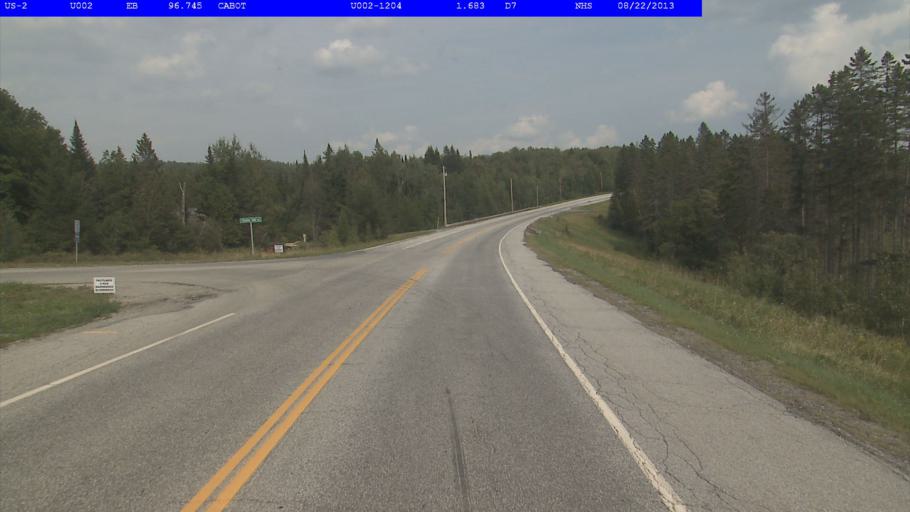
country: US
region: Vermont
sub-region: Caledonia County
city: Hardwick
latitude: 44.3666
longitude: -72.2926
